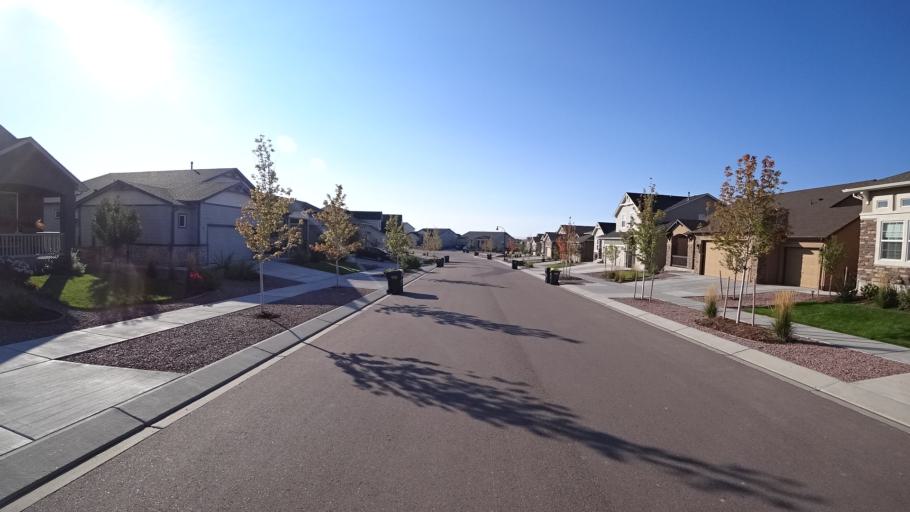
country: US
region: Colorado
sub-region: El Paso County
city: Cimarron Hills
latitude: 38.9348
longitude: -104.6622
